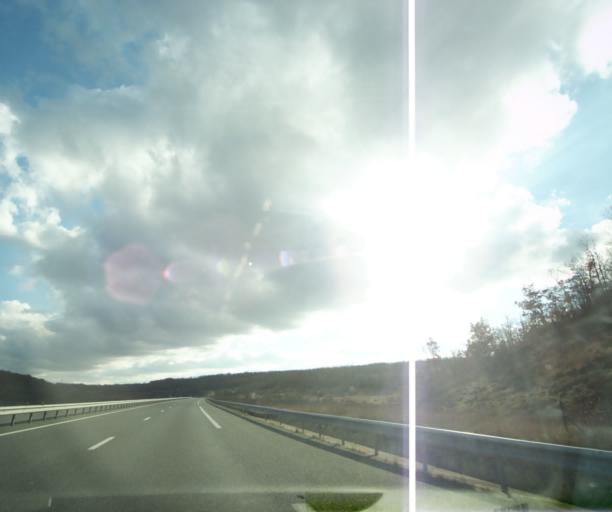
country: FR
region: Midi-Pyrenees
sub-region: Departement du Lot
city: Le Vigan
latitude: 44.7355
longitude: 1.5556
